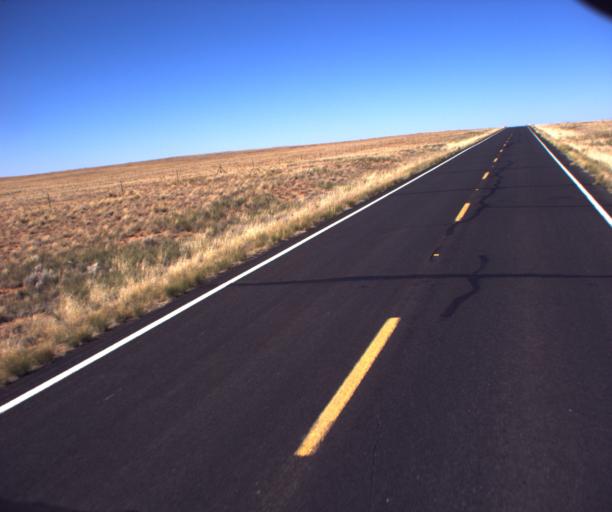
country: US
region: Arizona
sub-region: Navajo County
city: First Mesa
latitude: 35.6293
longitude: -110.4815
